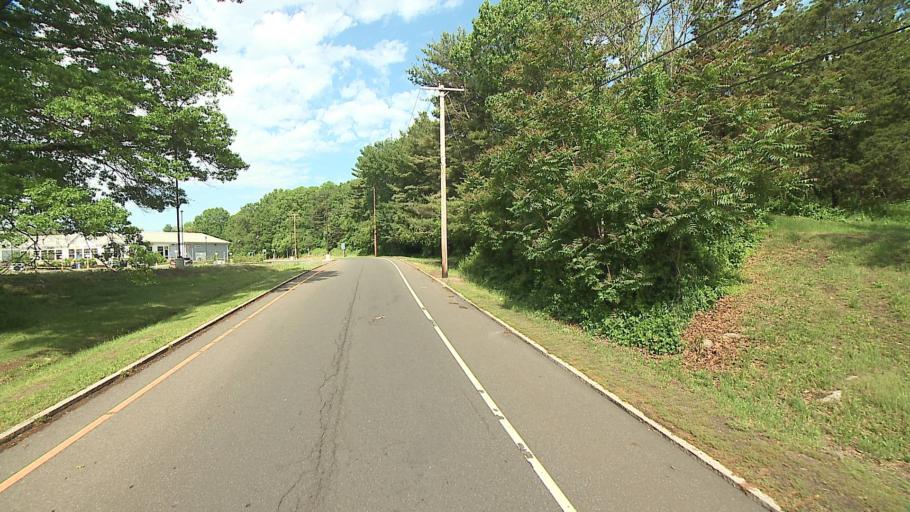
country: US
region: Connecticut
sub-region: Fairfield County
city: Fairfield
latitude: 41.1486
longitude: -73.2554
